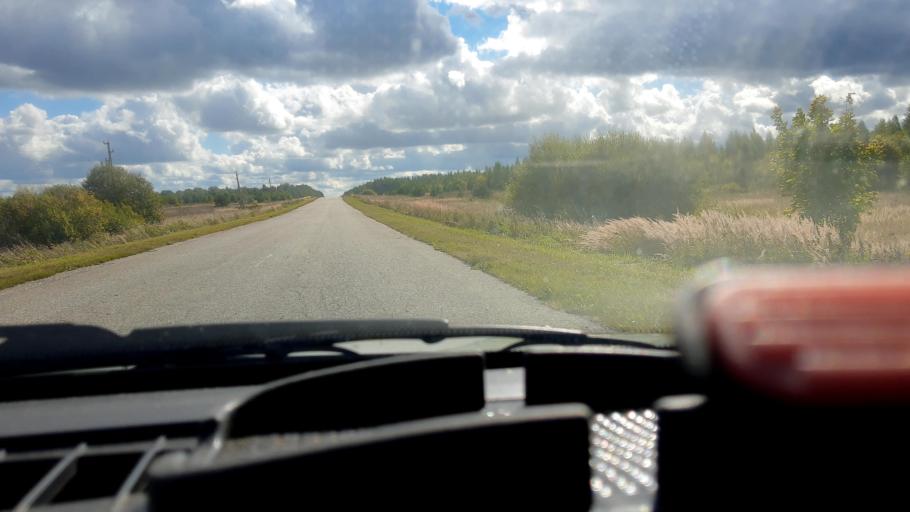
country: RU
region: Mariy-El
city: Kilemary
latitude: 56.9362
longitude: 46.6946
